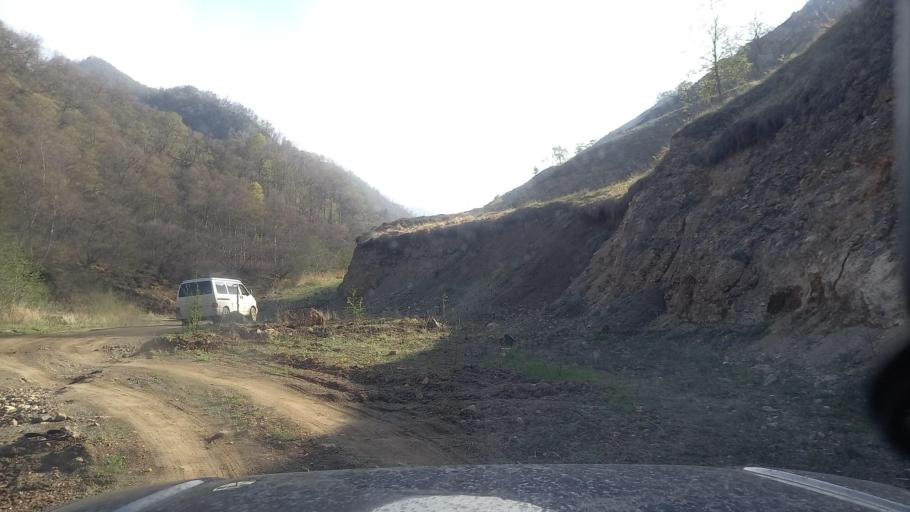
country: RU
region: Kabardino-Balkariya
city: Kamennomostskoye
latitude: 43.6975
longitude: 42.8407
